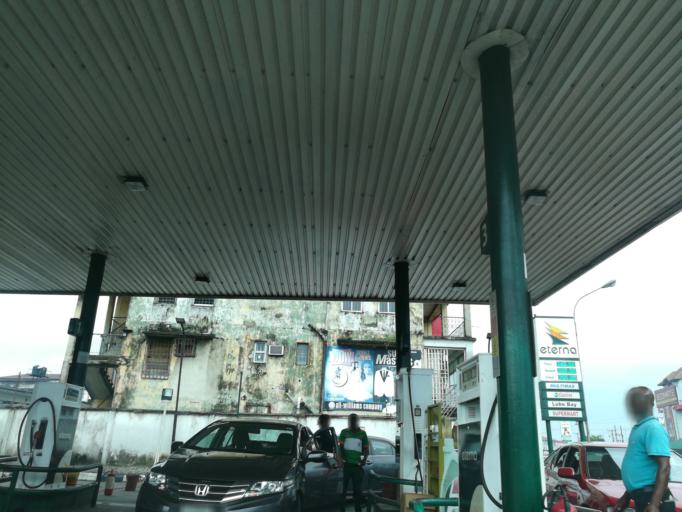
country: NG
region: Rivers
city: Port Harcourt
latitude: 4.7906
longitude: 7.0017
